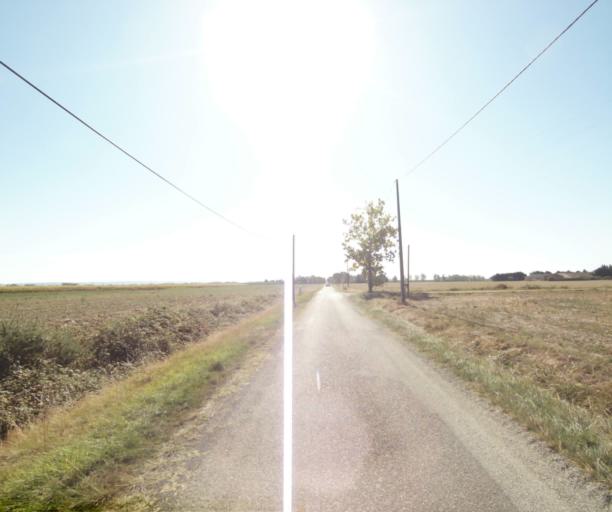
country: FR
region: Midi-Pyrenees
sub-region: Departement du Tarn-et-Garonne
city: Verdun-sur-Garonne
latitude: 43.8372
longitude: 1.2161
